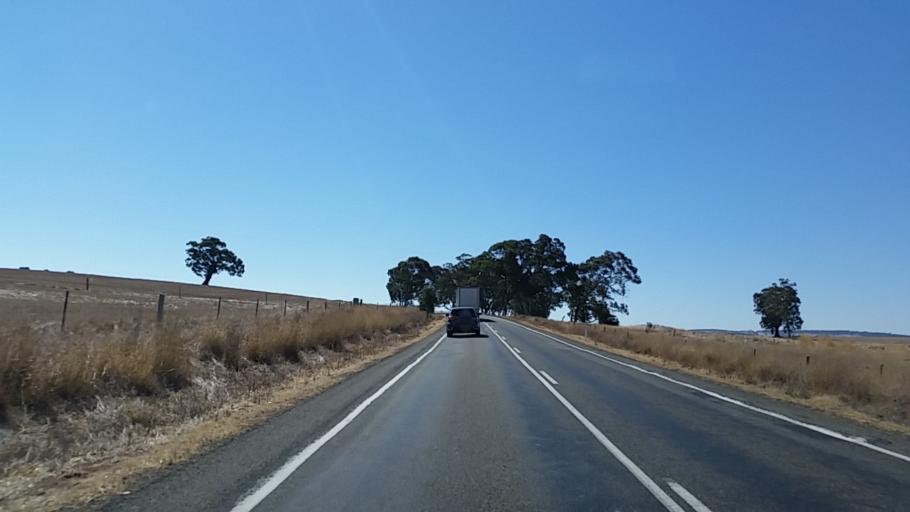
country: AU
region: South Australia
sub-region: Clare and Gilbert Valleys
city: Clare
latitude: -34.0398
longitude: 138.8009
